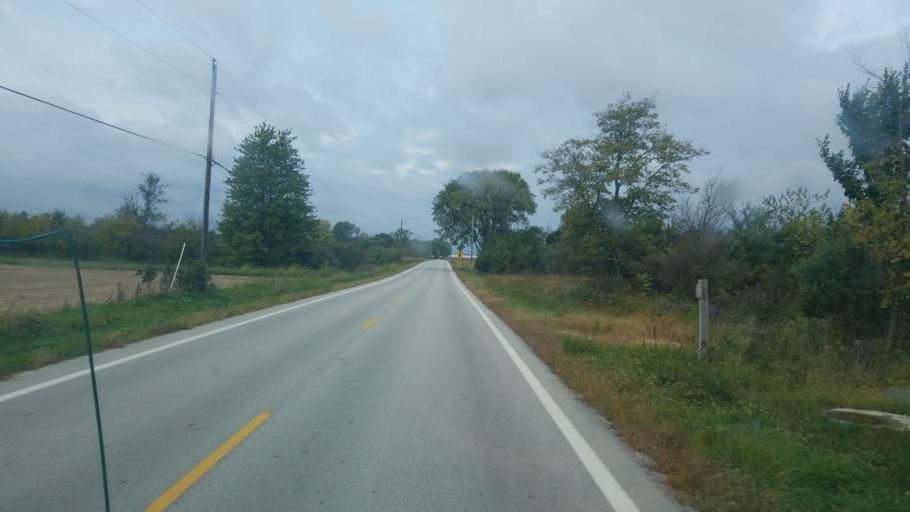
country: US
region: Ohio
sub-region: Wood County
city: North Baltimore
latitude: 41.1747
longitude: -83.5960
